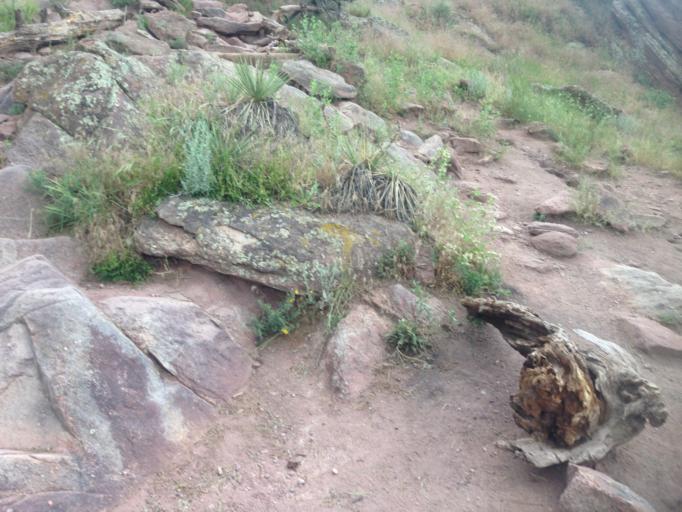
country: US
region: Colorado
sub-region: Boulder County
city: Boulder
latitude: 40.0276
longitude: -105.3010
